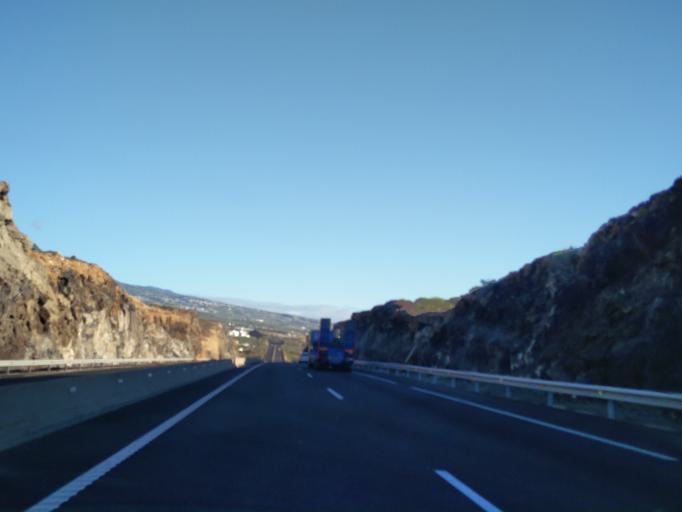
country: ES
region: Canary Islands
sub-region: Provincia de Santa Cruz de Tenerife
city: Fasnia
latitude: 28.1821
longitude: -16.4298
